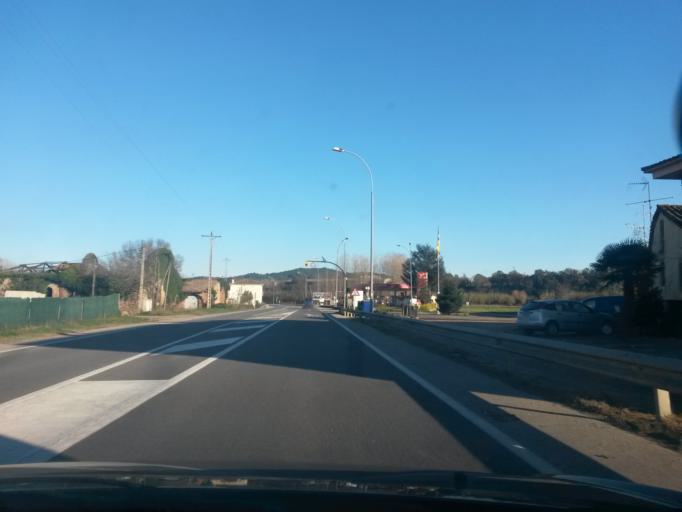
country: ES
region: Catalonia
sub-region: Provincia de Girona
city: Angles
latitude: 41.9584
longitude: 2.6471
